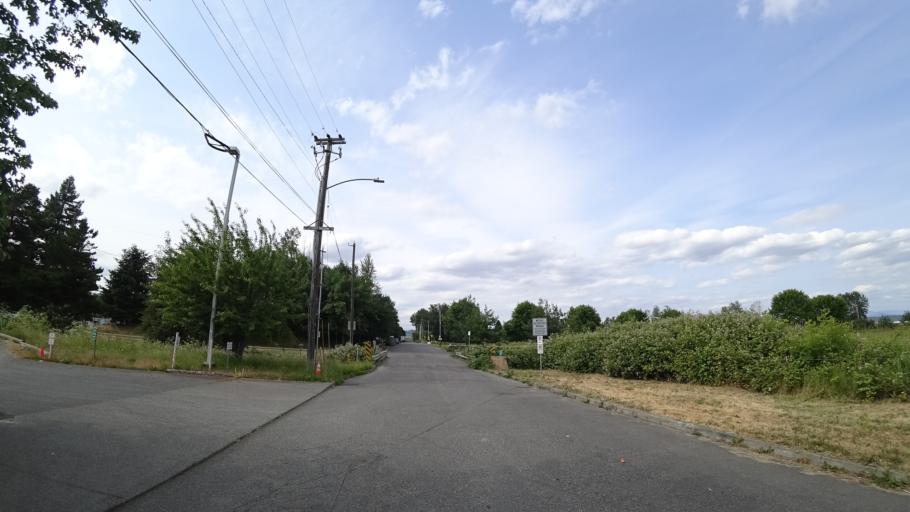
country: US
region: Washington
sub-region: Clark County
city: Vancouver
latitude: 45.5903
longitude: -122.6358
